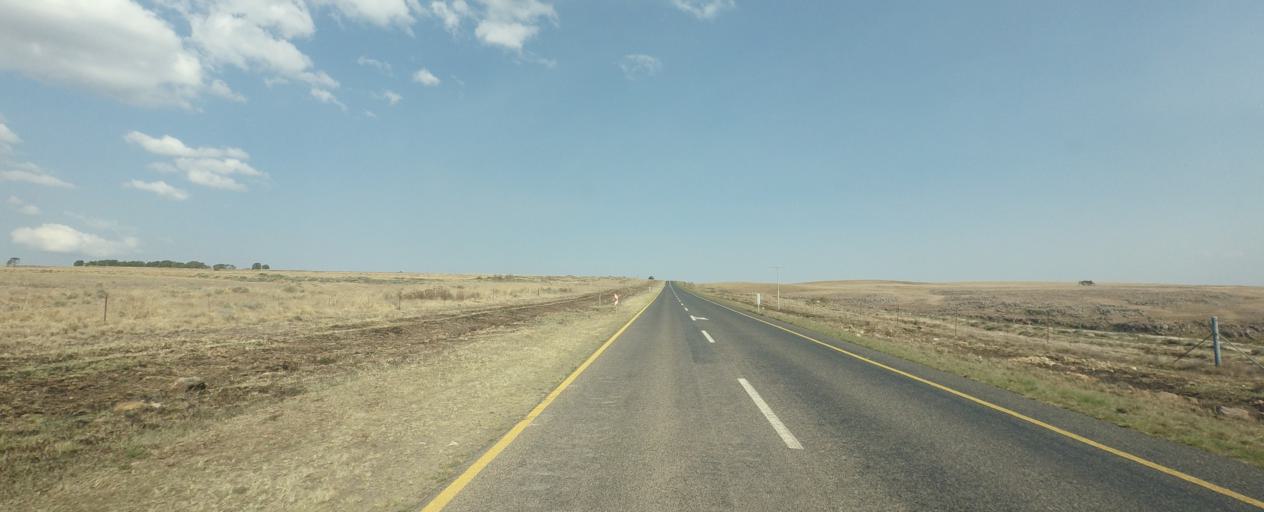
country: ZA
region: Mpumalanga
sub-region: Ehlanzeni District
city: Lydenburg
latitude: -25.1240
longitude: 30.5823
